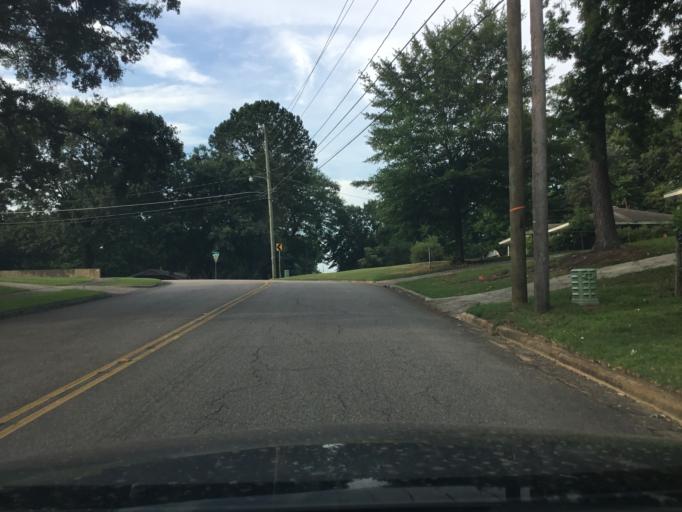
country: US
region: Alabama
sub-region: Montgomery County
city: Montgomery
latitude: 32.3744
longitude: -86.2566
